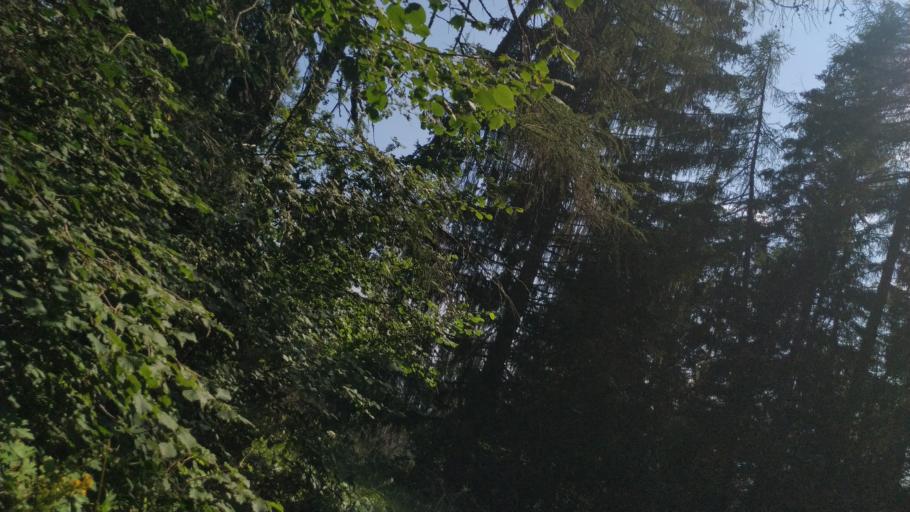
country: IT
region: Trentino-Alto Adige
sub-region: Bolzano
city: San Felice
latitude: 46.4859
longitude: 11.1529
